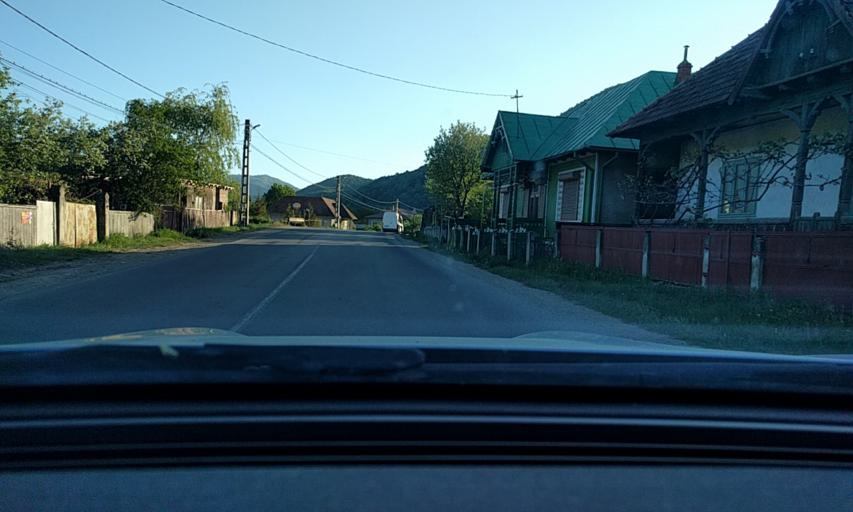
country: RO
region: Bacau
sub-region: Oras Slanic-Moldova
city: Slanic-Moldova
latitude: 46.1670
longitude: 26.4714
